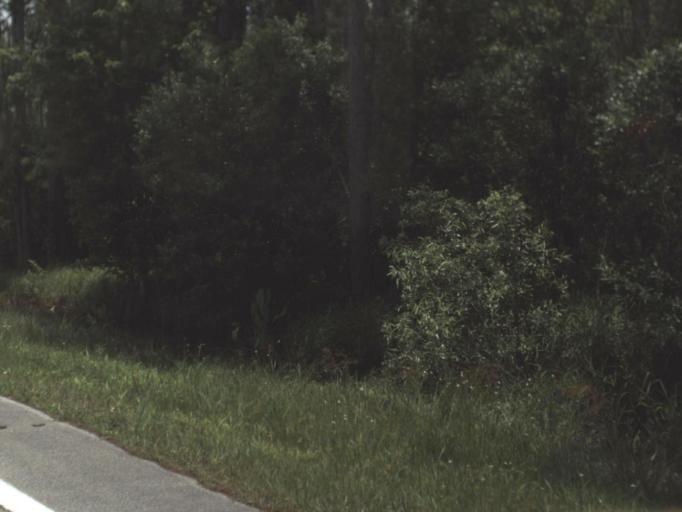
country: US
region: Florida
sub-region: Levy County
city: Bronson
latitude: 29.4147
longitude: -82.6806
